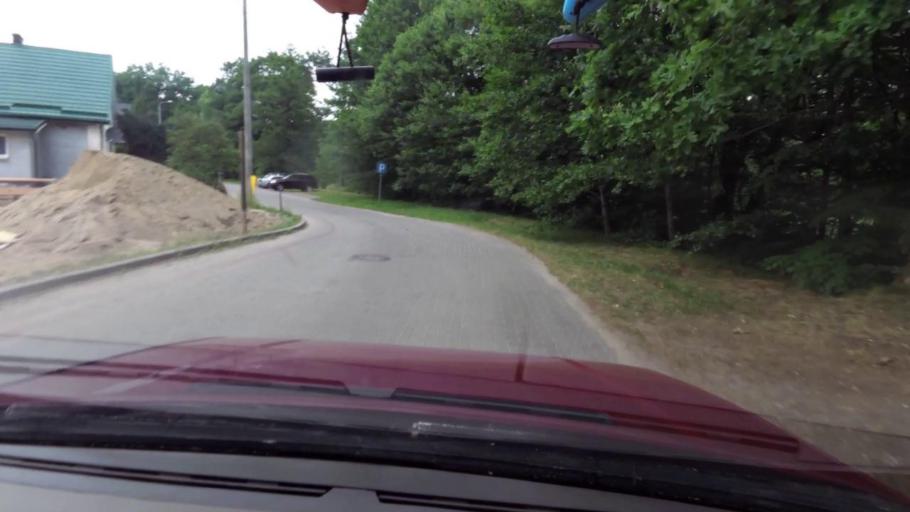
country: PL
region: Pomeranian Voivodeship
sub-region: Powiat slupski
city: Kepice
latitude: 54.2429
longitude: 16.8948
